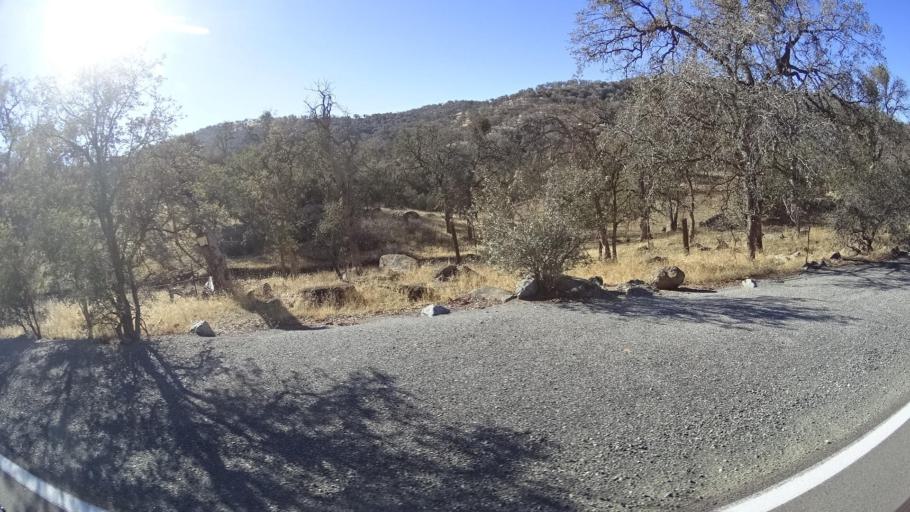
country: US
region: California
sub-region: Kern County
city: Alta Sierra
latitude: 35.7071
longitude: -118.7697
